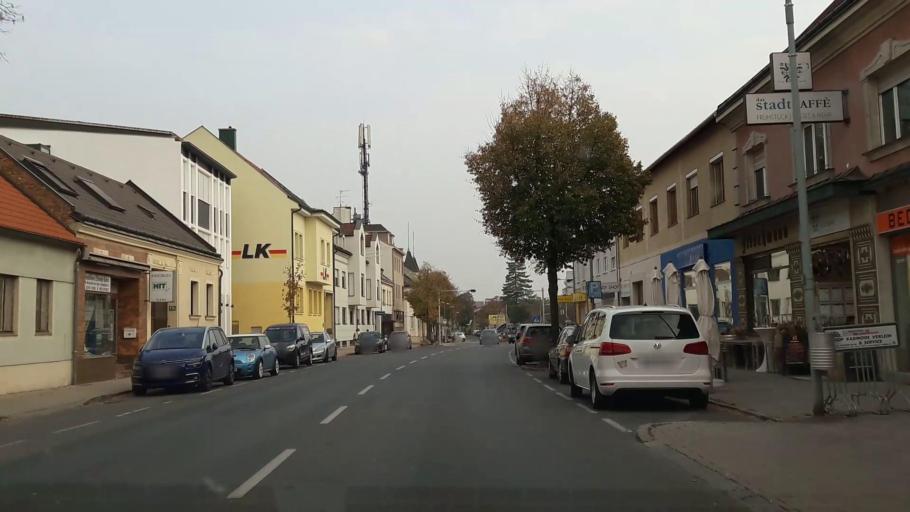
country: AT
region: Burgenland
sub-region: Politischer Bezirk Neusiedl am See
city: Neusiedl am See
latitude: 47.9466
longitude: 16.8466
